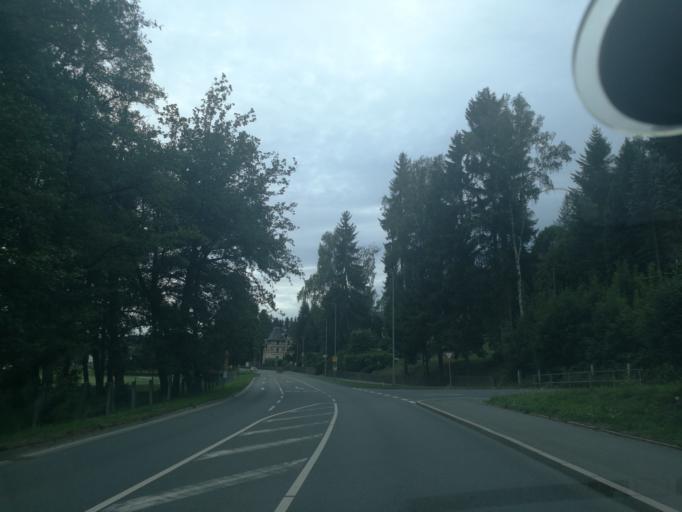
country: DE
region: Saxony
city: Adorf
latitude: 50.3128
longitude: 12.2526
